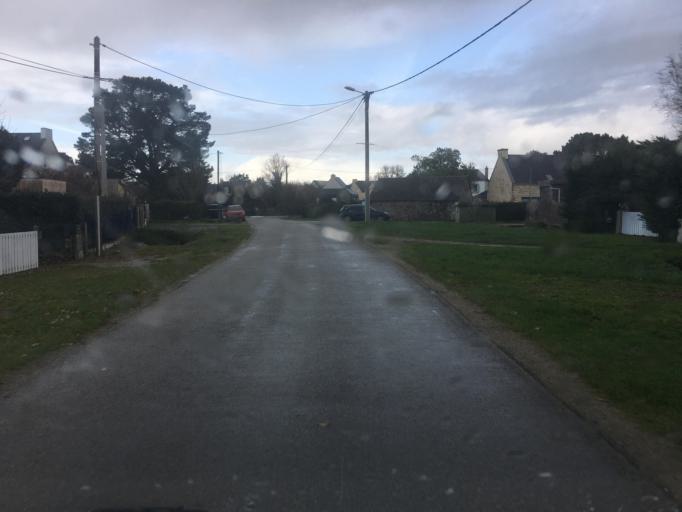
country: FR
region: Brittany
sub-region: Departement du Morbihan
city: Surzur
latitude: 47.5170
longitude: -2.6677
